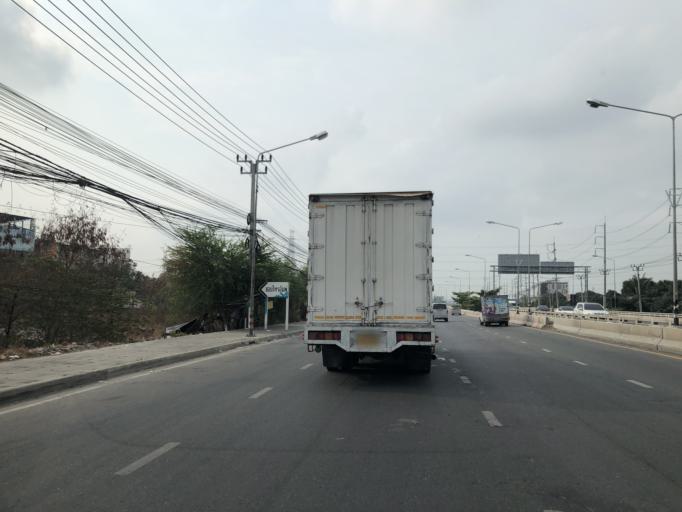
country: TH
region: Bangkok
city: Bang Na
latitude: 13.5993
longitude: 100.6994
